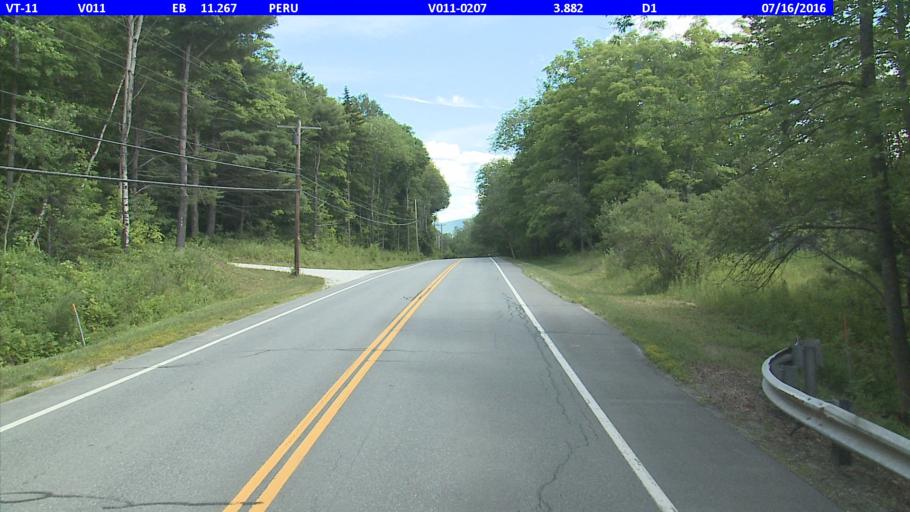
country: US
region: Vermont
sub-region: Bennington County
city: Manchester Center
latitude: 43.2351
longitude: -72.8793
